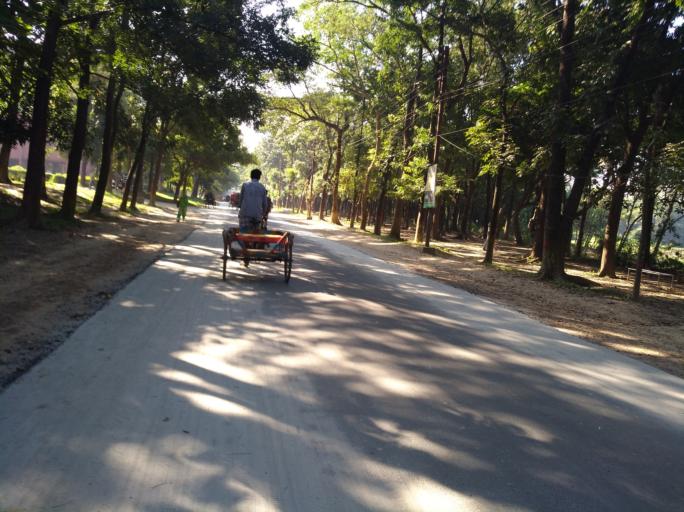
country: BD
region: Dhaka
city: Tungi
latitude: 23.8834
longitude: 90.2678
